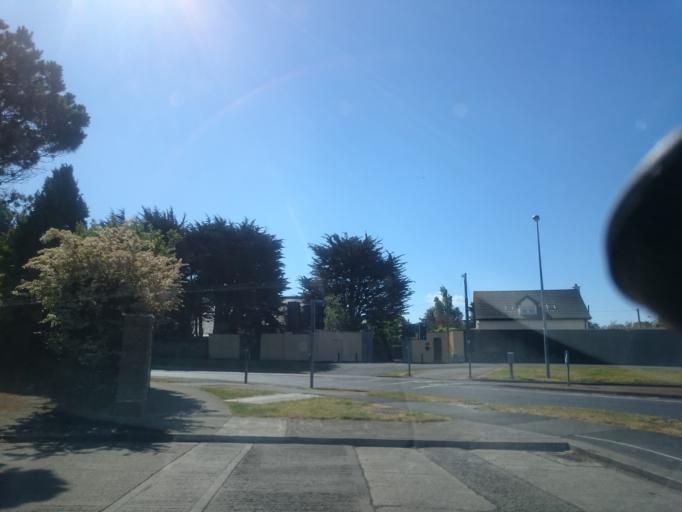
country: IE
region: Leinster
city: Sallynoggin
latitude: 53.2667
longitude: -6.1343
